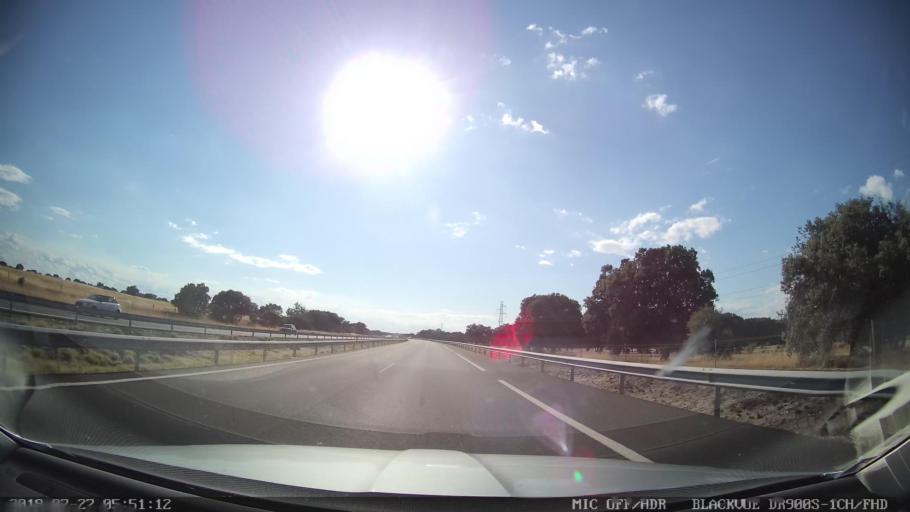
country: ES
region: Castille-La Mancha
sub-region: Province of Toledo
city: Alcanizo
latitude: 39.9230
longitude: -5.0929
